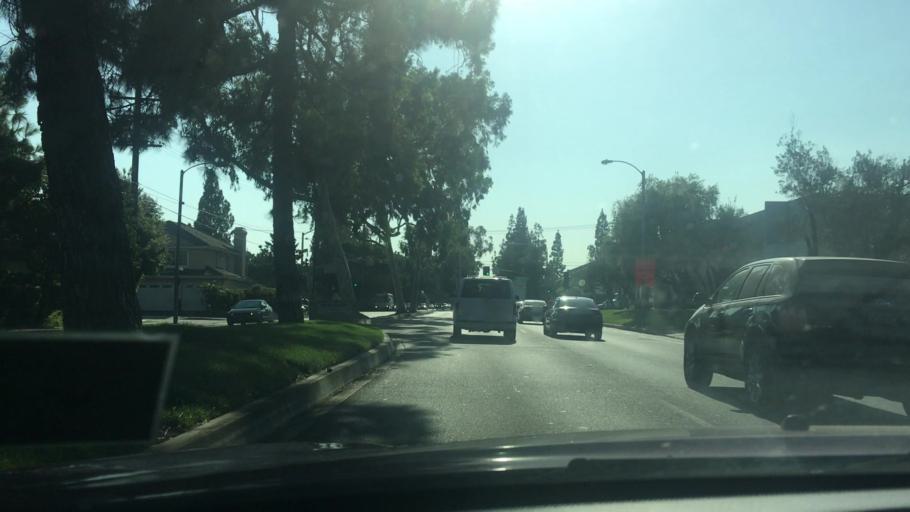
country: US
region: California
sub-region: Orange County
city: La Palma
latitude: 33.8733
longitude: -118.0366
